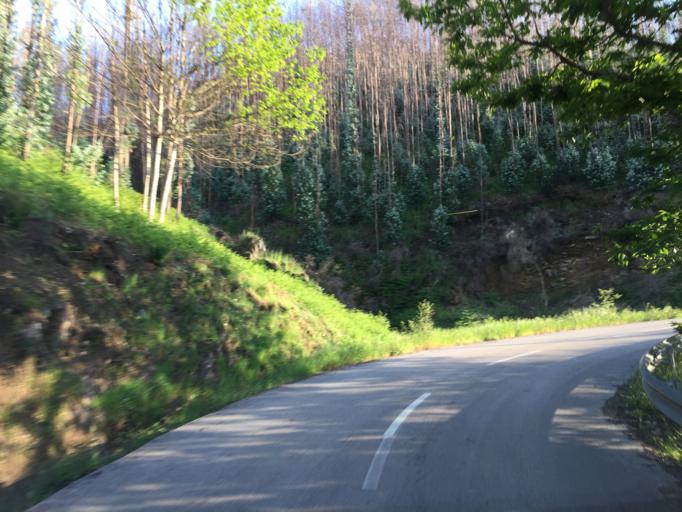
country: PT
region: Coimbra
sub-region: Arganil
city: Arganil
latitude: 40.1302
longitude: -8.0073
